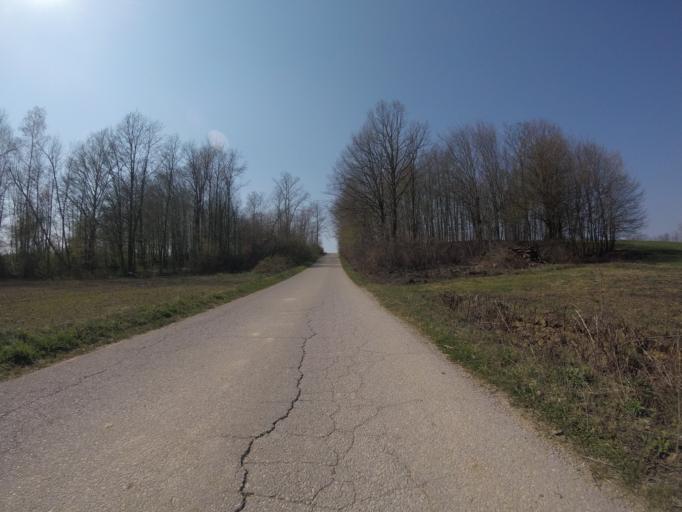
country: HR
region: Grad Zagreb
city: Strmec
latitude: 45.5585
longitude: 15.9162
